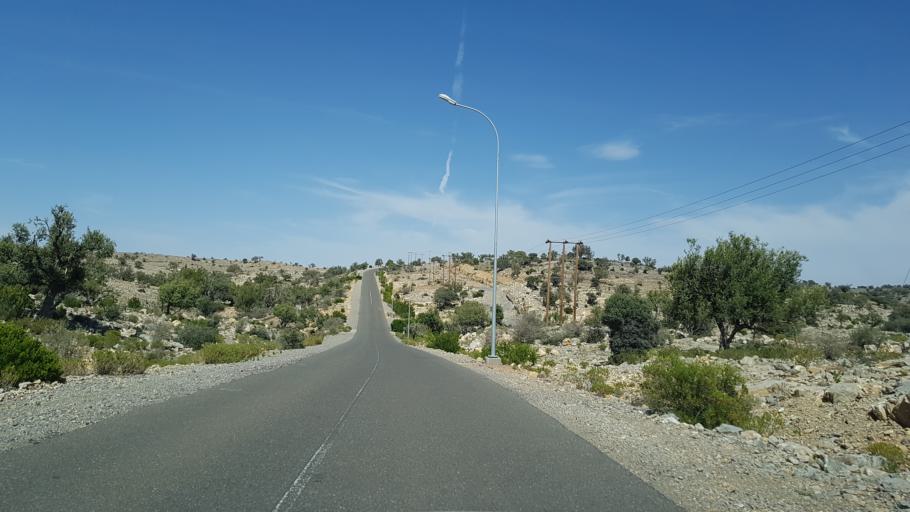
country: OM
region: Muhafazat ad Dakhiliyah
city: Nizwa
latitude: 23.1200
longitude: 57.6073
